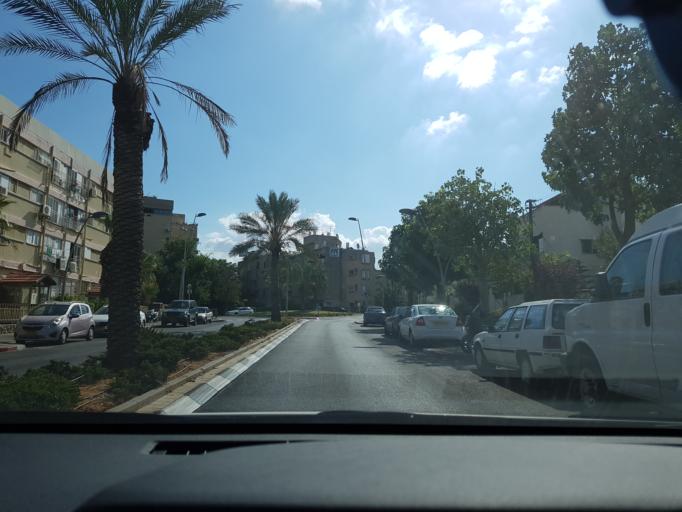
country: IL
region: Tel Aviv
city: Holon
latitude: 32.0117
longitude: 34.7920
